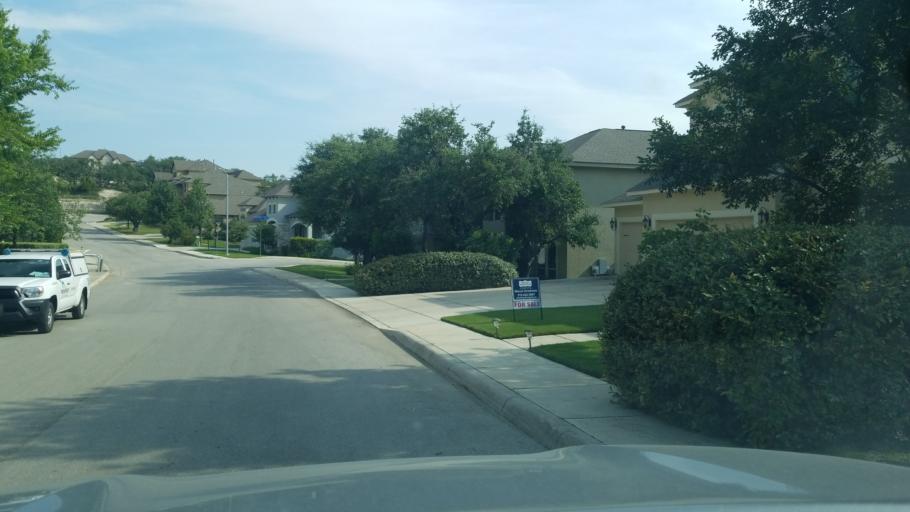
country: US
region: Texas
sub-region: Bexar County
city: Scenic Oaks
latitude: 29.7156
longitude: -98.6558
